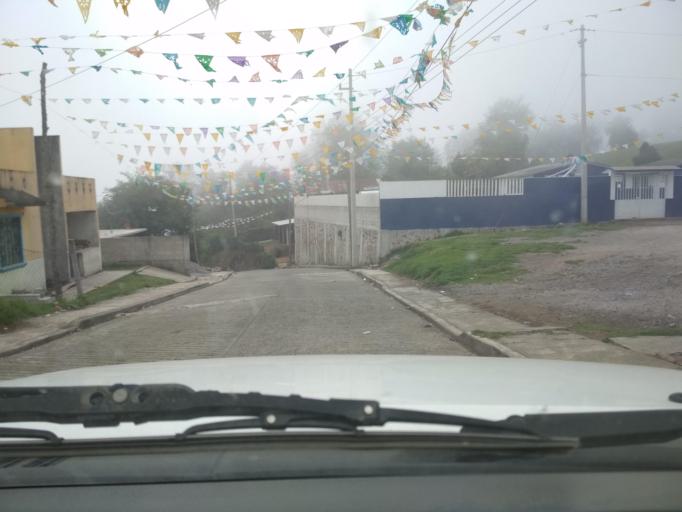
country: MX
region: Veracruz
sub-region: La Perla
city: Chilapa
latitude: 18.9992
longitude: -97.1611
